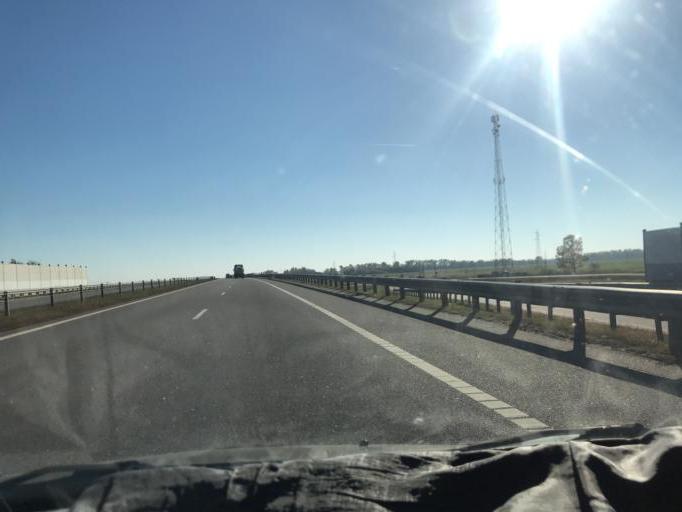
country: BY
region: Mogilev
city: Yalizava
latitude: 53.2484
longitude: 28.9300
